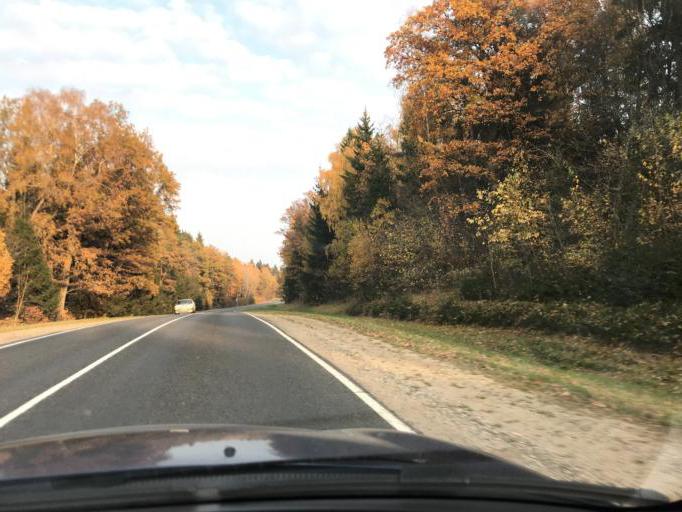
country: BY
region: Grodnenskaya
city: Navahrudak
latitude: 53.5887
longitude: 25.9003
